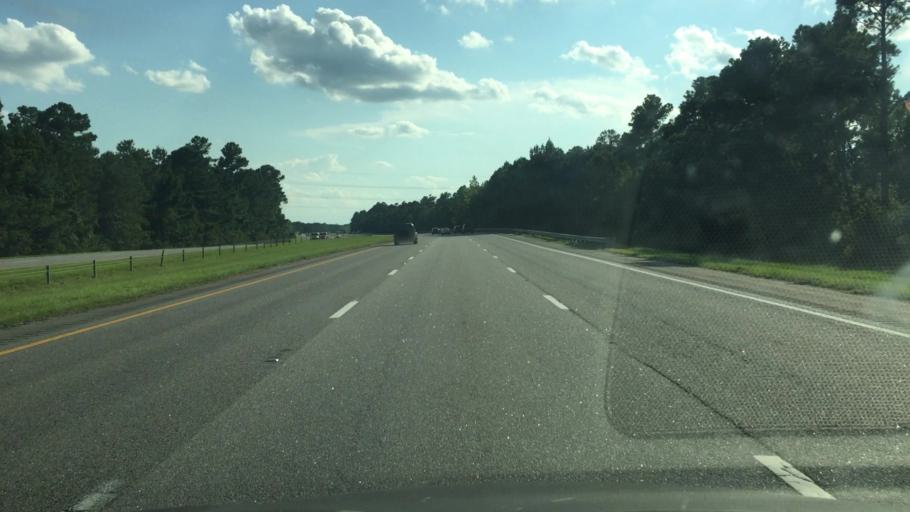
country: US
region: South Carolina
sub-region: Horry County
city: Myrtle Beach
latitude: 33.7668
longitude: -78.8313
